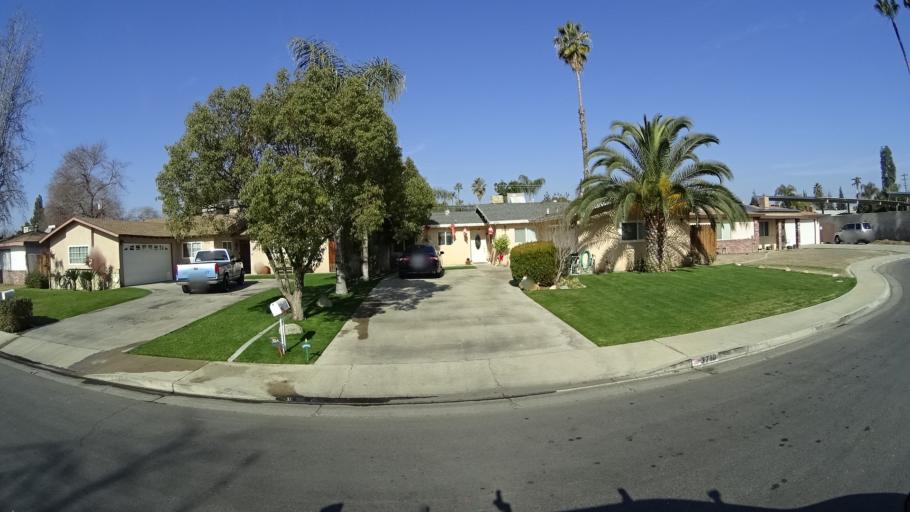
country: US
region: California
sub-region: Kern County
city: Bakersfield
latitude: 35.3355
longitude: -119.0447
